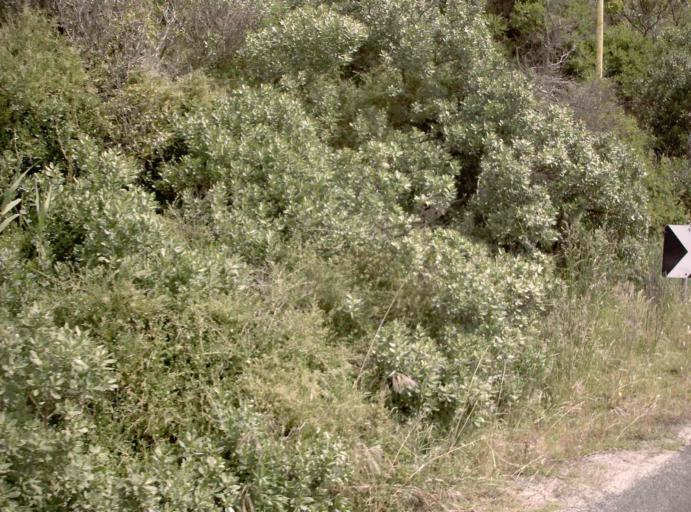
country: AU
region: Victoria
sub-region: Mornington Peninsula
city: McCrae
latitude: -38.3416
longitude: 144.9439
